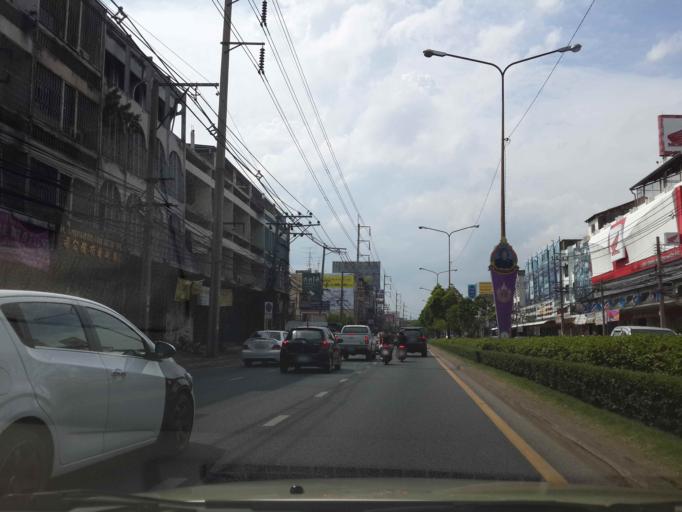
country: TH
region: Bangkok
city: Bang Kapi
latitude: 13.7586
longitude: 100.6457
